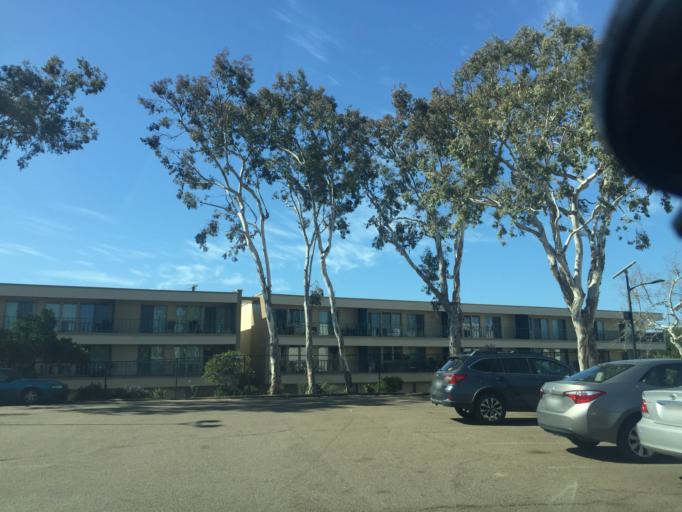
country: US
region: California
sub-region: San Diego County
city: San Diego
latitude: 32.7938
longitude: -117.1940
